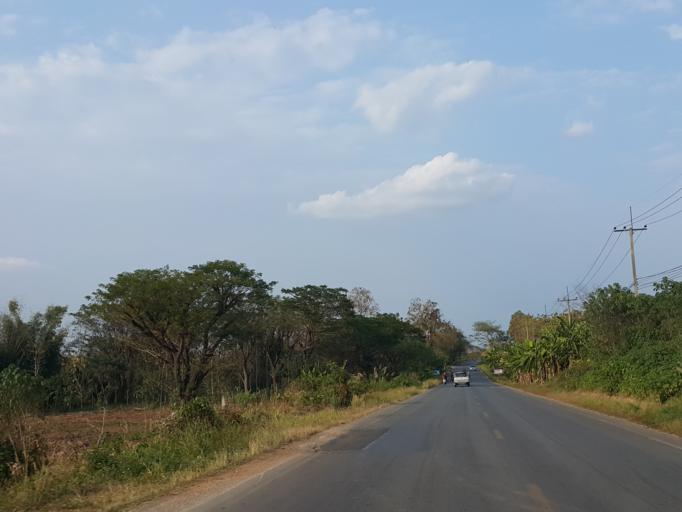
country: TH
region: Lampang
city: Hang Chat
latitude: 18.4440
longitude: 99.4507
